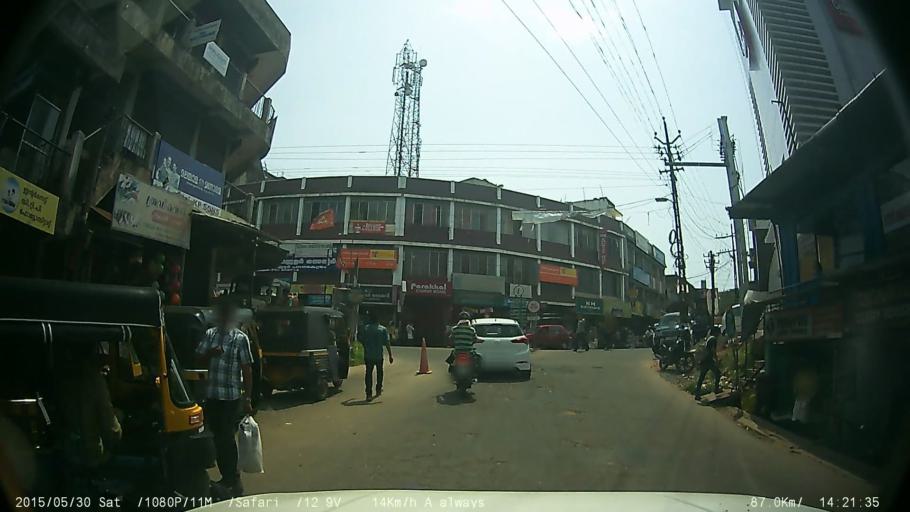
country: IN
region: Kerala
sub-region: Wayanad
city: Panamaram
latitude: 11.8029
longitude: 76.0064
